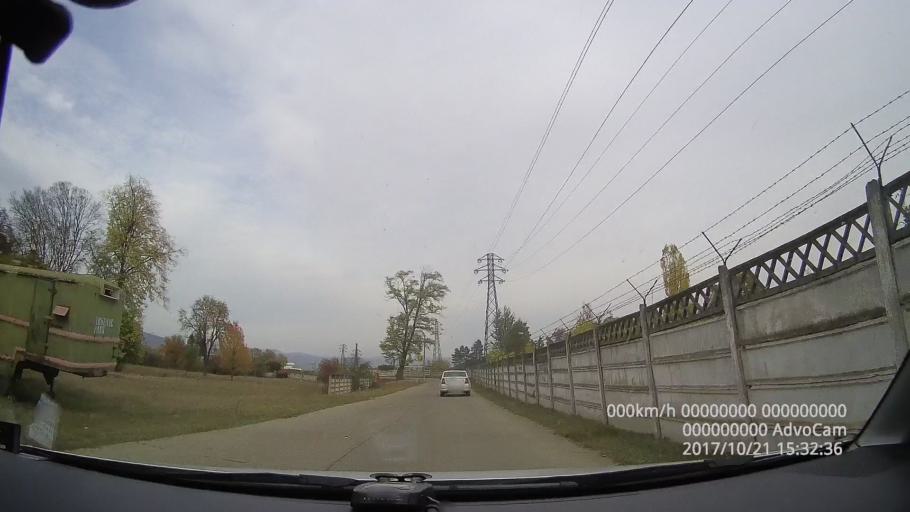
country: RO
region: Hunedoara
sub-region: Comuna Soimus
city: Soimus
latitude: 45.9019
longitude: 22.8856
